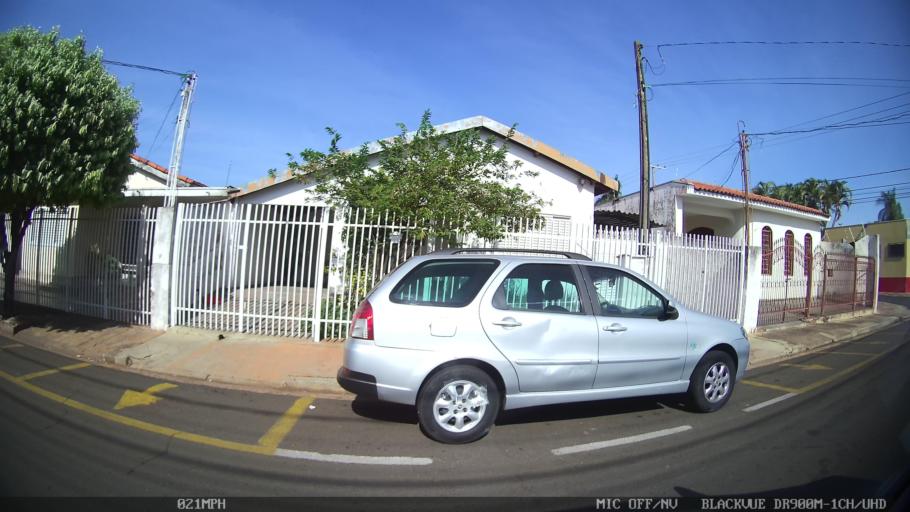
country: BR
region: Sao Paulo
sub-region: Sao Jose Do Rio Preto
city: Sao Jose do Rio Preto
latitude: -20.8082
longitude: -49.3978
